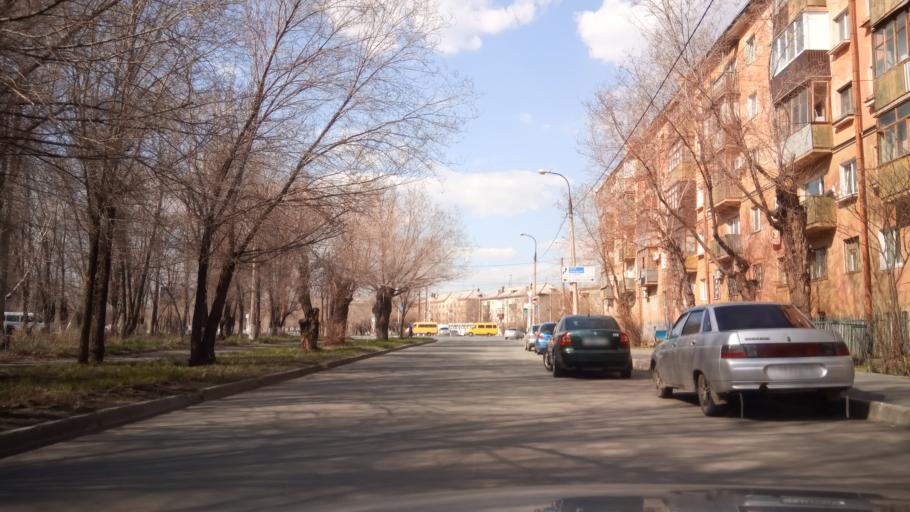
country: RU
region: Orenburg
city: Novotroitsk
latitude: 51.1952
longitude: 58.3015
